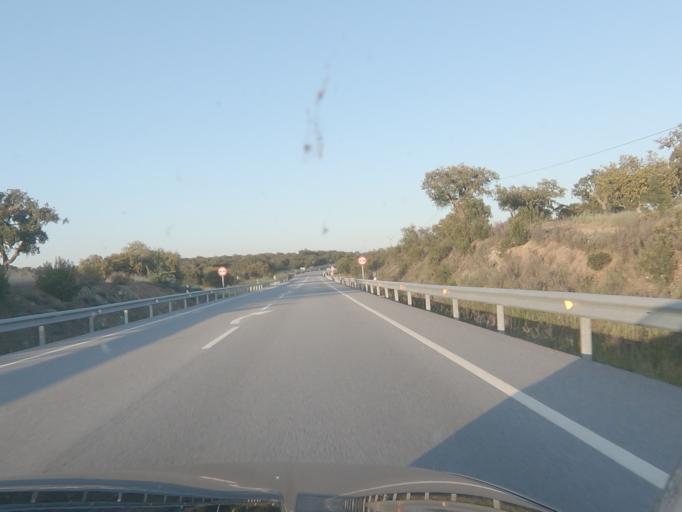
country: ES
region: Extremadura
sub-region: Provincia de Caceres
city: Carbajo
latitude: 39.5064
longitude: -7.1500
